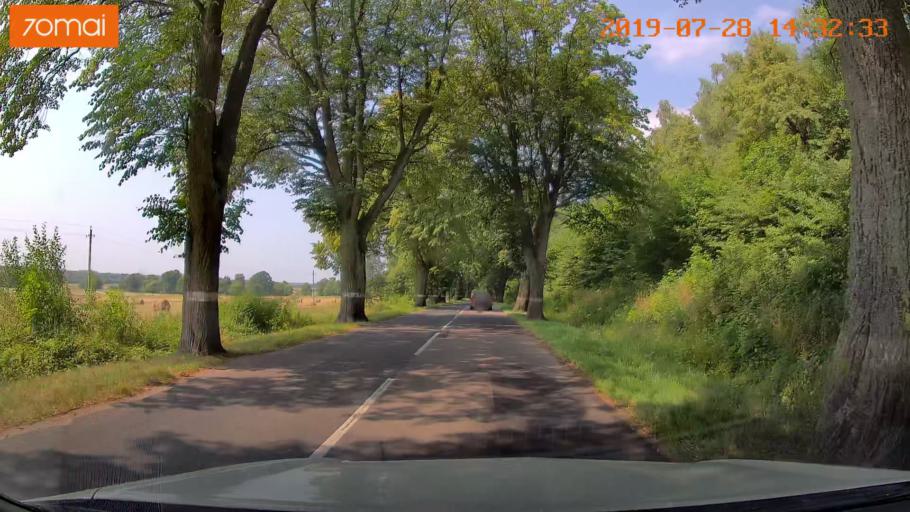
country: RU
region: Kaliningrad
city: Primorsk
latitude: 54.8134
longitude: 20.0405
